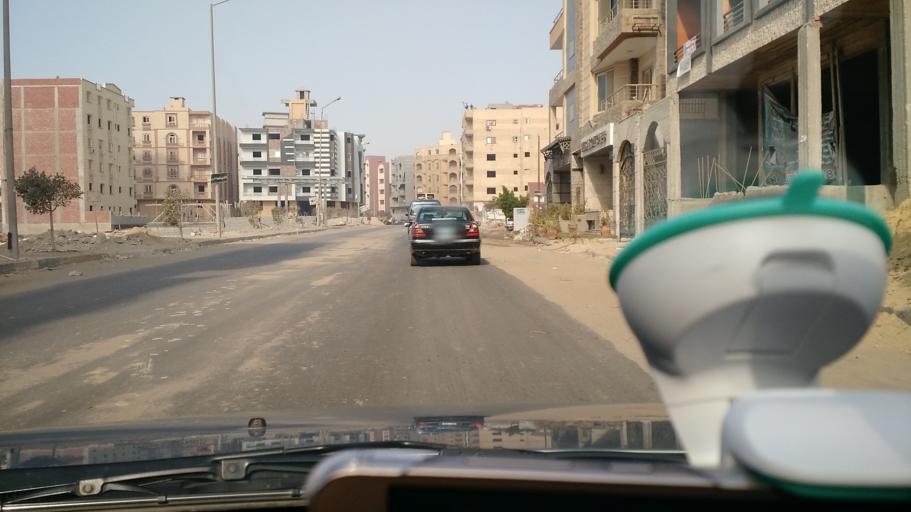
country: EG
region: Muhafazat al Qahirah
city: Cairo
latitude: 30.0047
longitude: 31.2879
